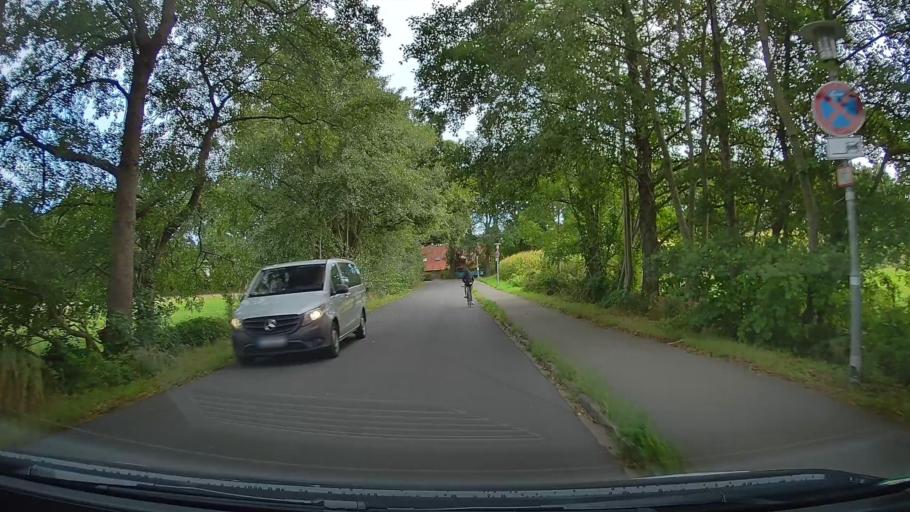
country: DE
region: Lower Saxony
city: Oldenburg
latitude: 53.1491
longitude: 8.1673
